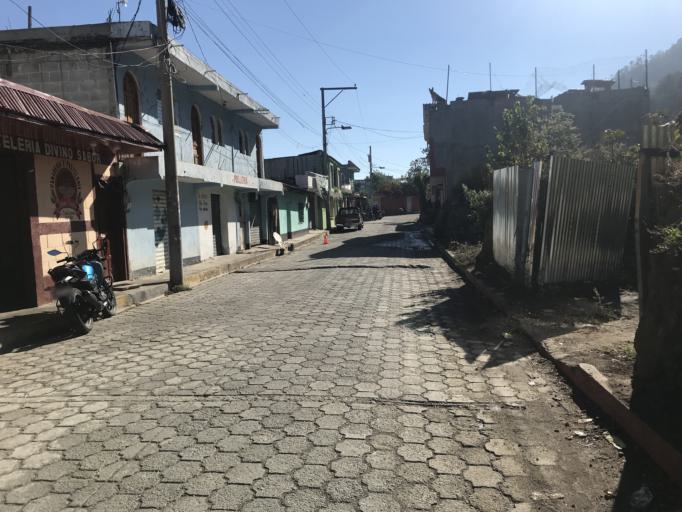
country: GT
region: San Marcos
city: San Miguel Ixtahuacan
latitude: 15.2721
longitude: -91.7477
